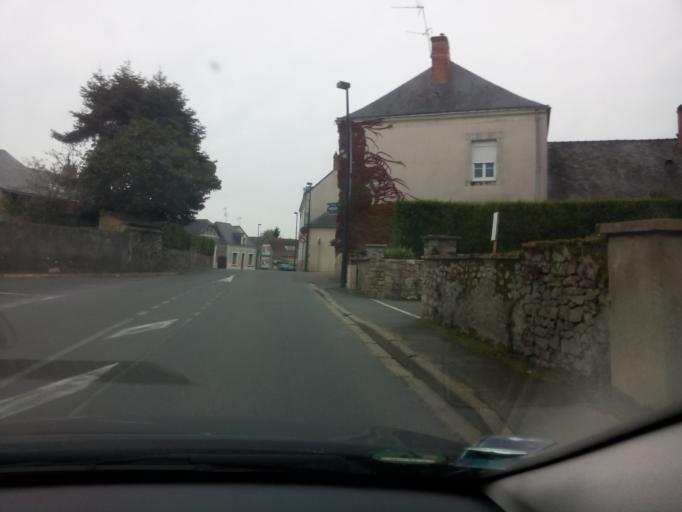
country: FR
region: Pays de la Loire
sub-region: Departement de Maine-et-Loire
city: Seiches-sur-le-Loir
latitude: 47.5758
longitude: -0.3630
